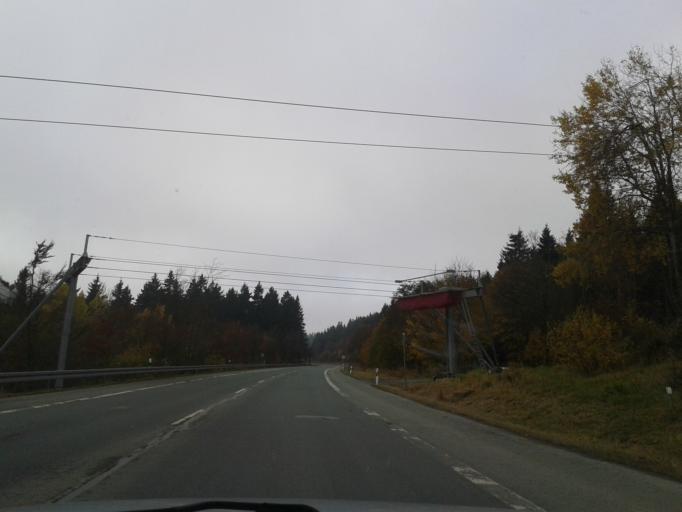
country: DE
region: North Rhine-Westphalia
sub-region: Regierungsbezirk Arnsberg
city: Winterberg
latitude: 51.1856
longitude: 8.5004
